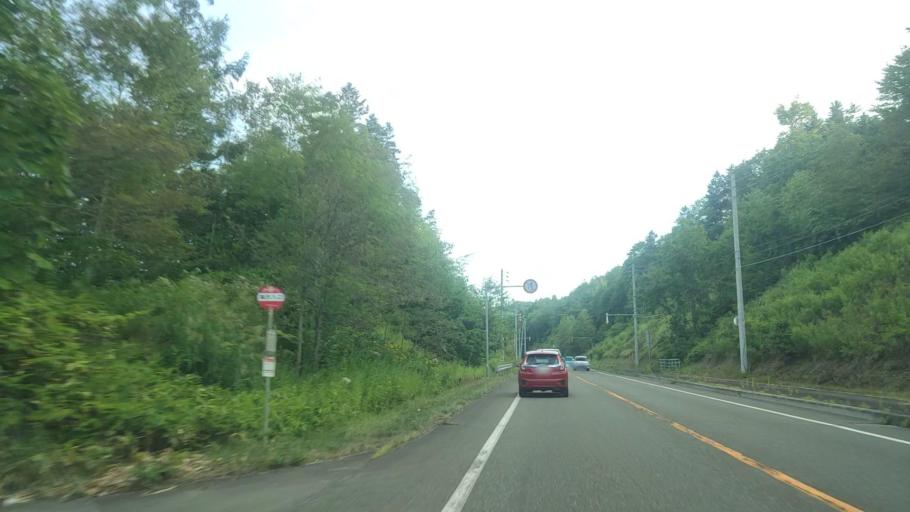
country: JP
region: Hokkaido
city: Iwamizawa
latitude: 43.0297
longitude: 141.9425
